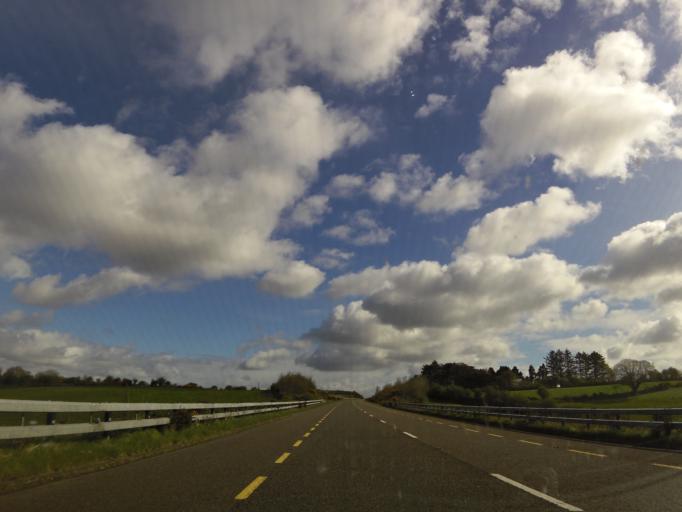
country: IE
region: Connaught
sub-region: Maigh Eo
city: Claremorris
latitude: 53.7824
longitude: -8.9443
